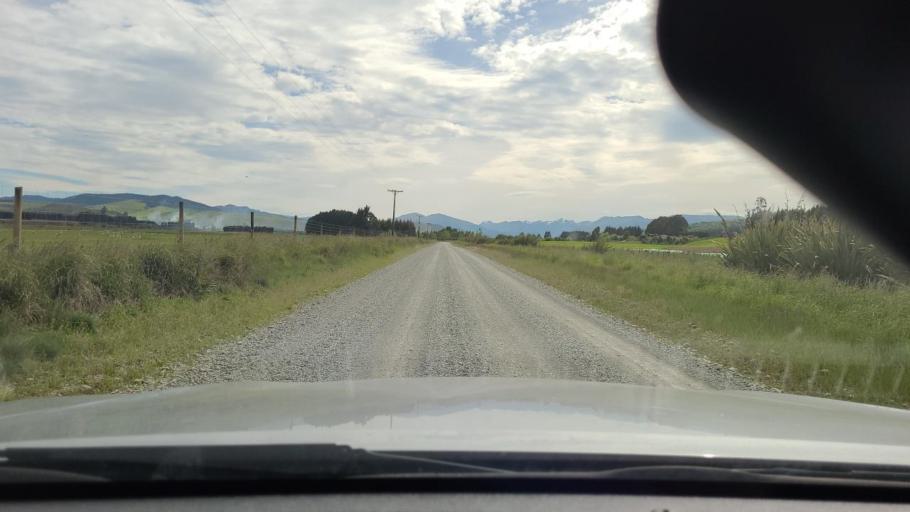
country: NZ
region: Southland
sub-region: Southland District
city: Te Anau
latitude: -45.5247
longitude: 167.9635
